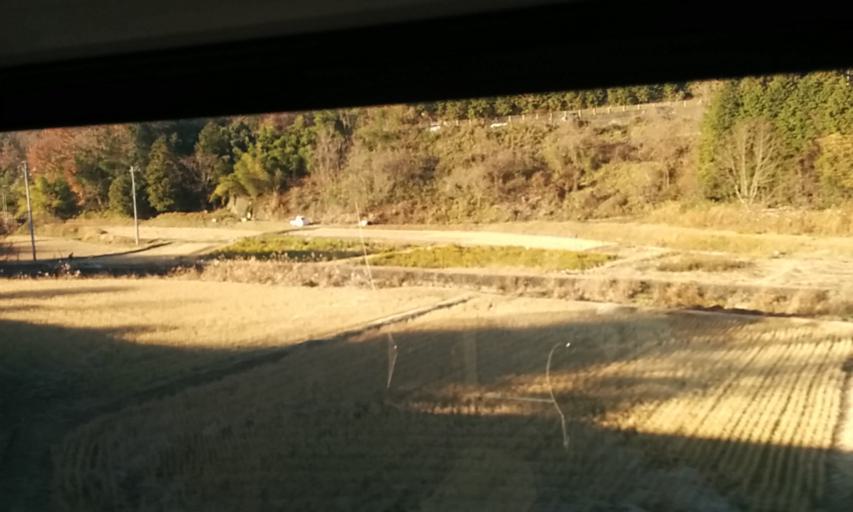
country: JP
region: Gifu
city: Mizunami
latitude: 35.4389
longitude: 137.3647
